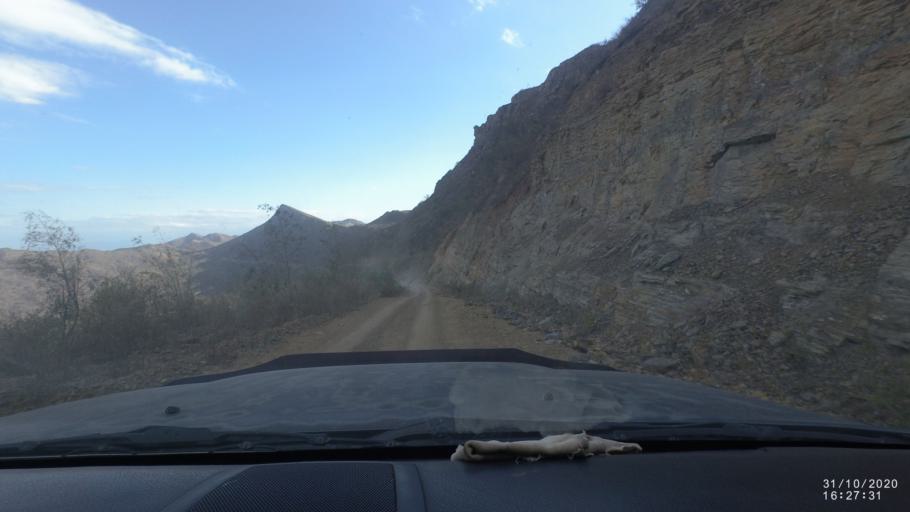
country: BO
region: Chuquisaca
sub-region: Provincia Zudanez
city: Mojocoya
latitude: -18.4067
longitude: -64.5861
